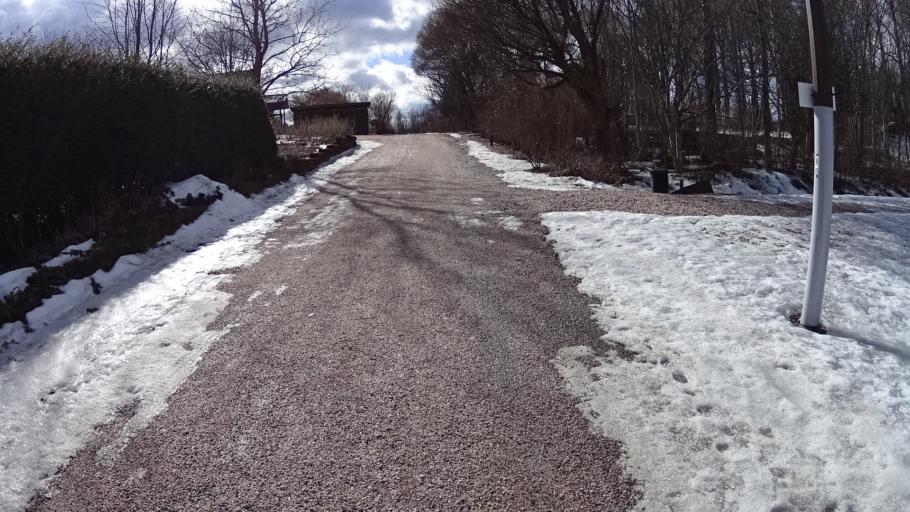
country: FI
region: Uusimaa
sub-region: Helsinki
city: Kauniainen
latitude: 60.2485
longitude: 24.7048
